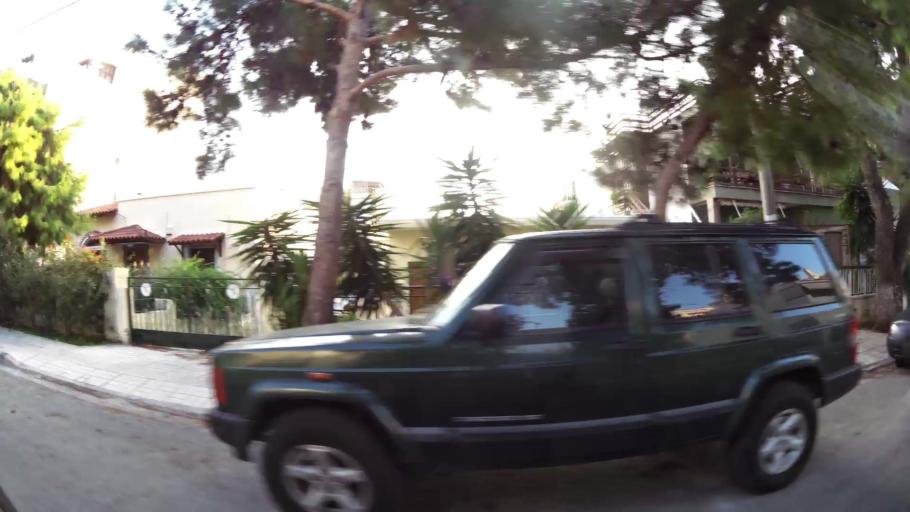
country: GR
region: Attica
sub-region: Nomarchia Athinas
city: Glyfada
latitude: 37.8865
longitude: 23.7672
